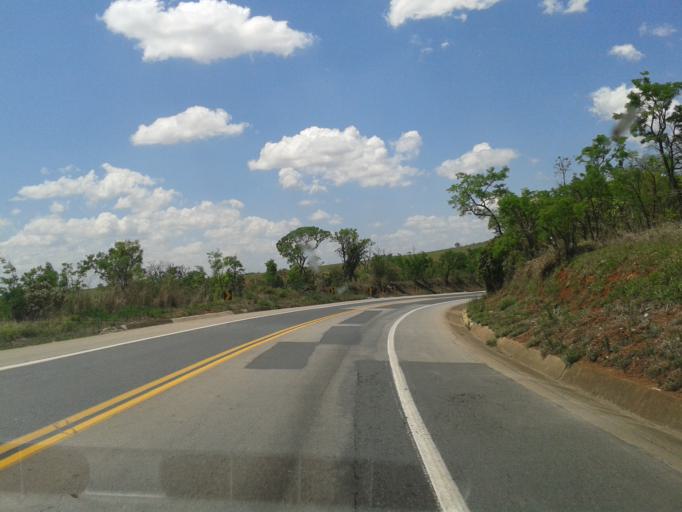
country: BR
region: Minas Gerais
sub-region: Ibia
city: Ibia
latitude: -19.5654
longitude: -46.6515
